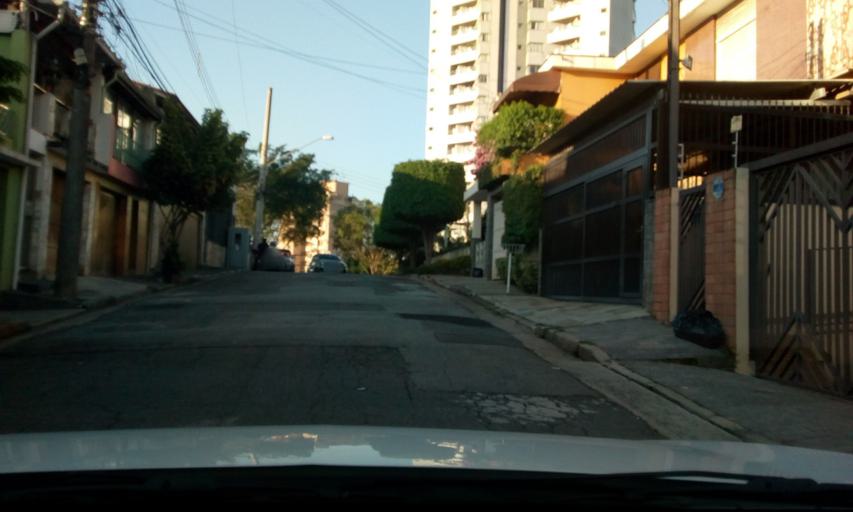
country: BR
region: Sao Paulo
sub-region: Sao Paulo
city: Sao Paulo
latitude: -23.4888
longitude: -46.6138
